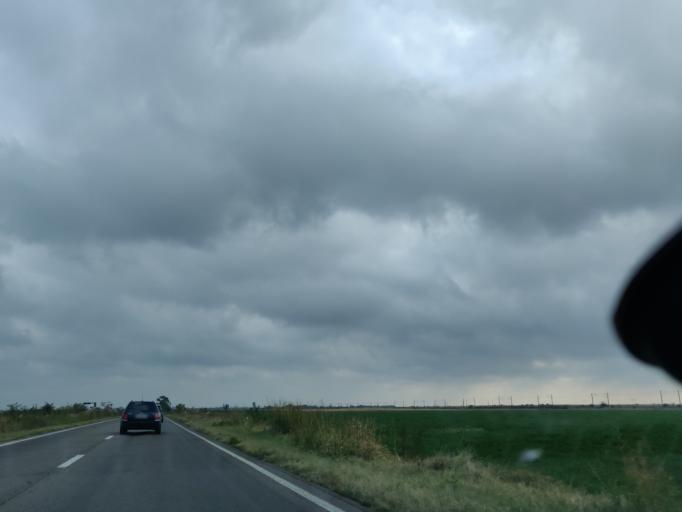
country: RO
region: Prahova
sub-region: Oras Mizil
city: Mizil
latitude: 45.0175
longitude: 26.4809
